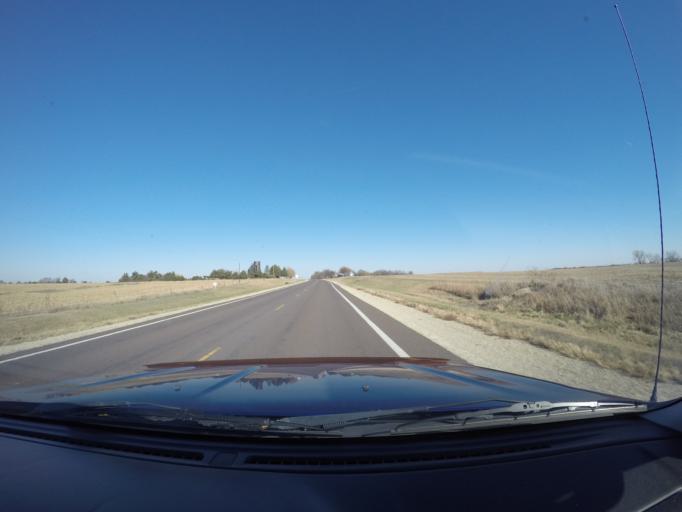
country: US
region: Kansas
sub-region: Marshall County
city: Blue Rapids
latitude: 39.5922
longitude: -96.7500
